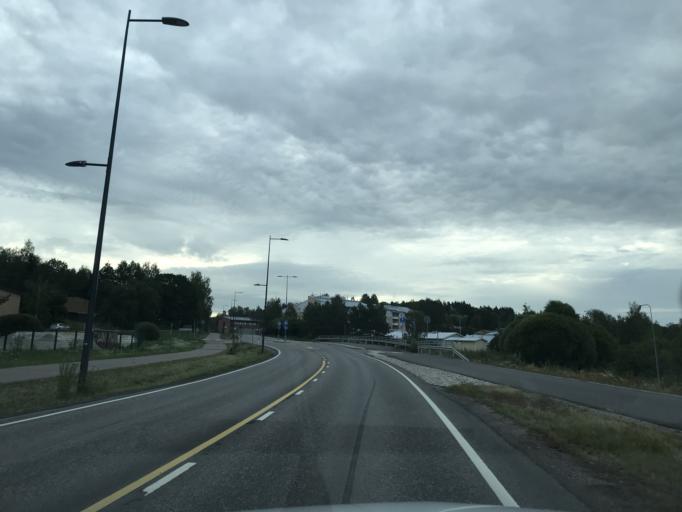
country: FI
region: Uusimaa
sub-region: Helsinki
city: Nurmijaervi
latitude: 60.3792
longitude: 24.7398
